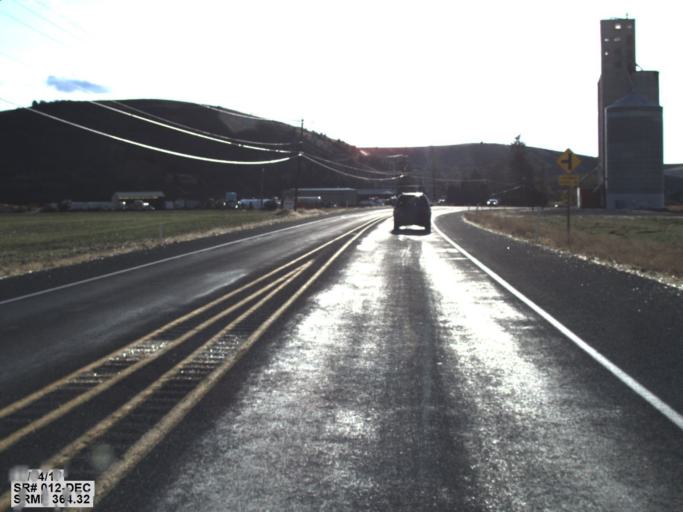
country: US
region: Washington
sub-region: Columbia County
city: Dayton
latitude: 46.2928
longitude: -118.0248
